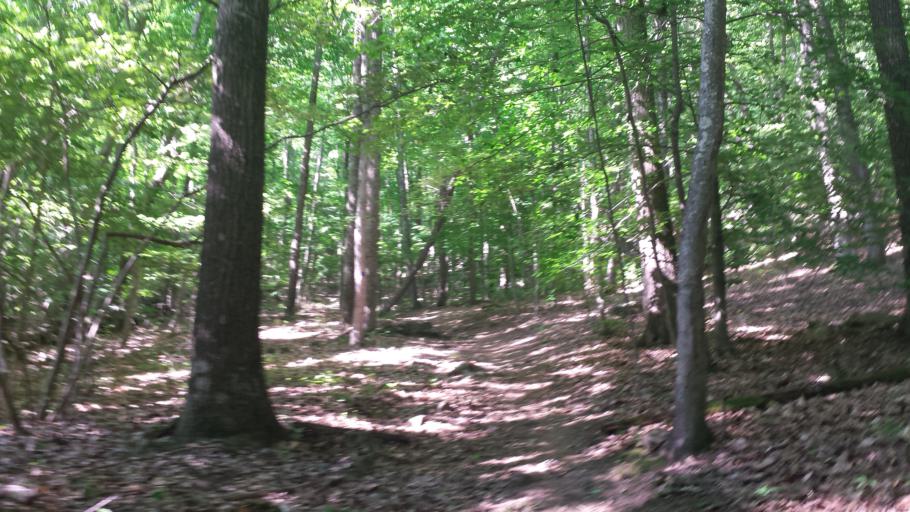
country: US
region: New York
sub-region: Westchester County
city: Pound Ridge
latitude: 41.2575
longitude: -73.5775
